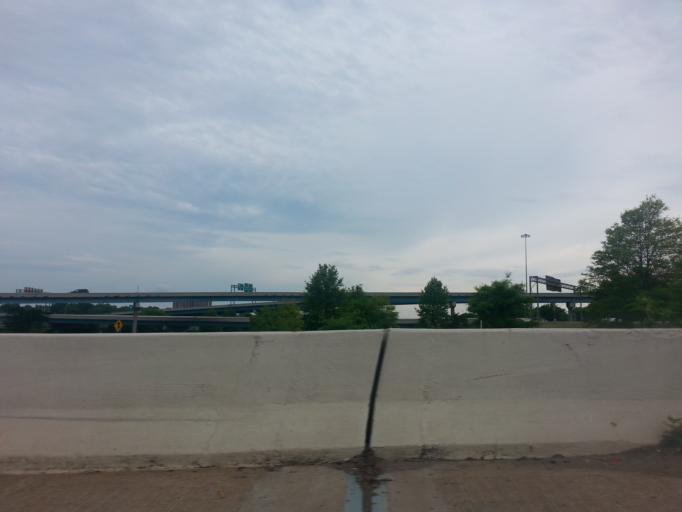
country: US
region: Tennessee
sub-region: Knox County
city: Knoxville
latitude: 35.9697
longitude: -83.9279
